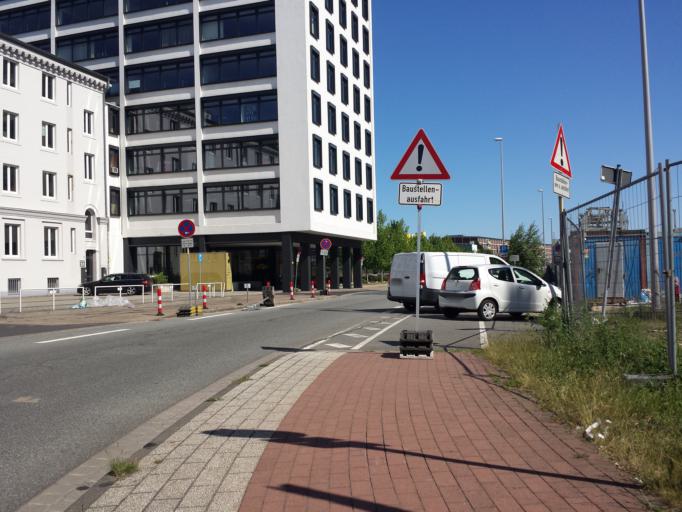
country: DE
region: Bremen
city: Bremen
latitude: 53.0940
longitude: 8.7716
